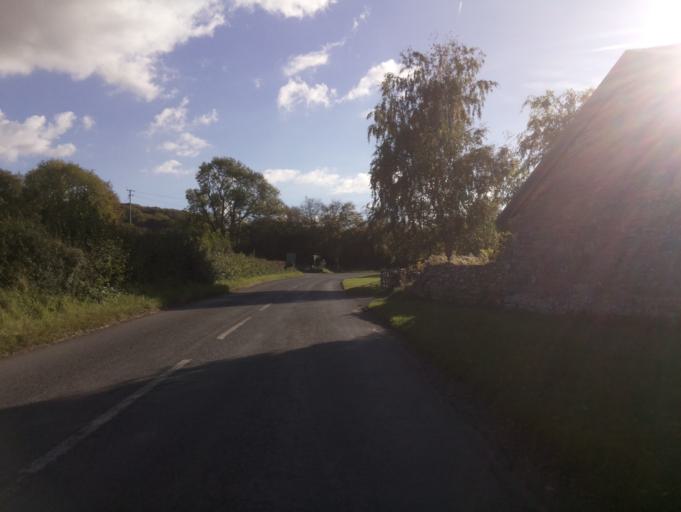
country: GB
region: England
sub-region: Herefordshire
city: Clifford
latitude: 52.1070
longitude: -3.0994
